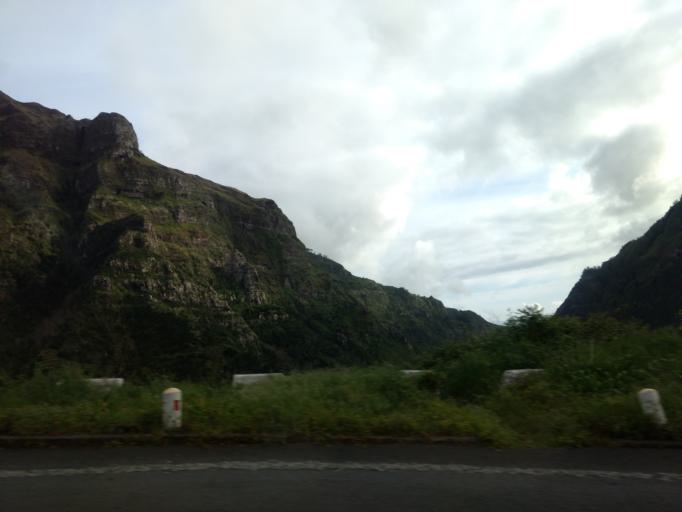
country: PT
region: Madeira
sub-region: Camara de Lobos
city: Curral das Freiras
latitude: 32.7309
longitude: -17.0248
